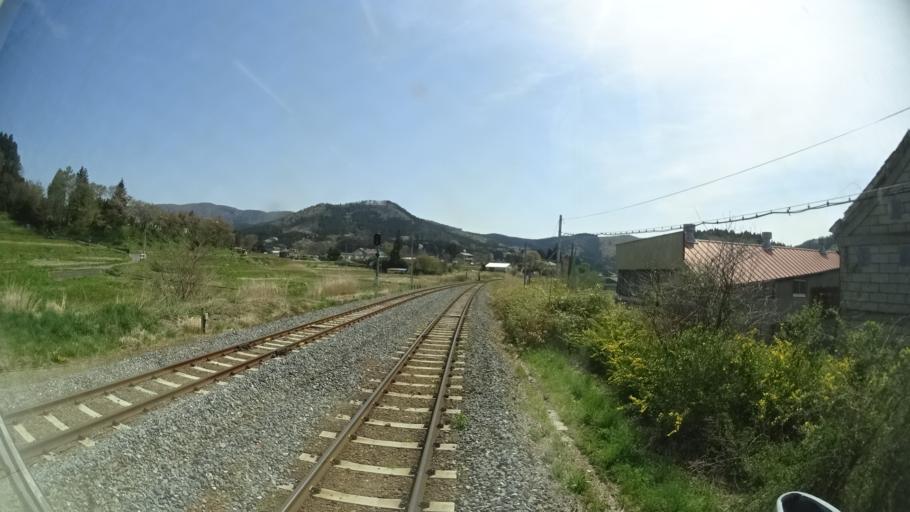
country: JP
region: Iwate
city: Ofunato
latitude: 38.9396
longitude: 141.4531
